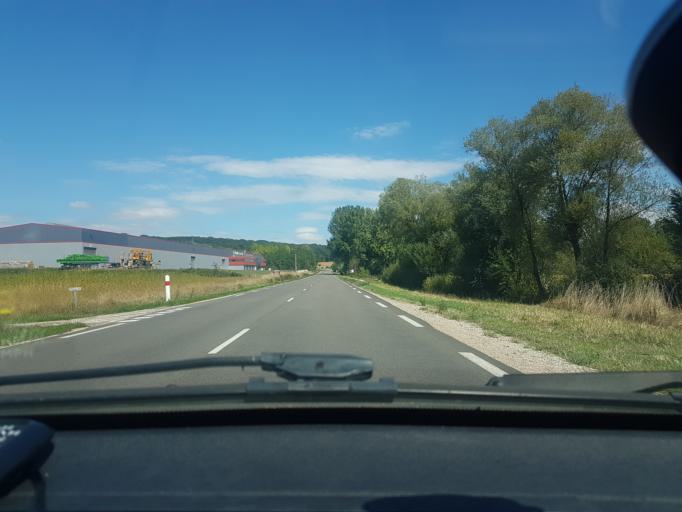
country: FR
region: Franche-Comte
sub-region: Departement de la Haute-Saone
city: Gray-la-Ville
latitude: 47.4413
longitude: 5.5476
